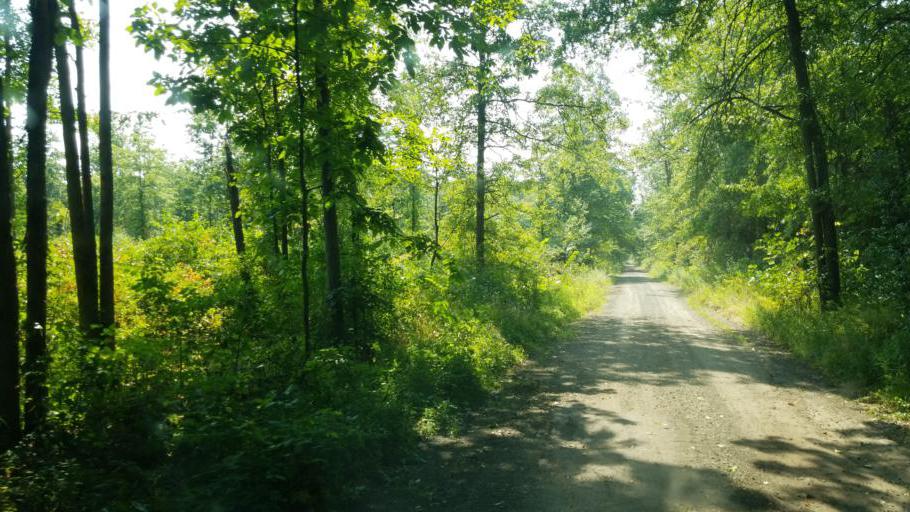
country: US
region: Ohio
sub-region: Ashtabula County
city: Orwell
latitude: 41.4926
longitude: -80.9047
